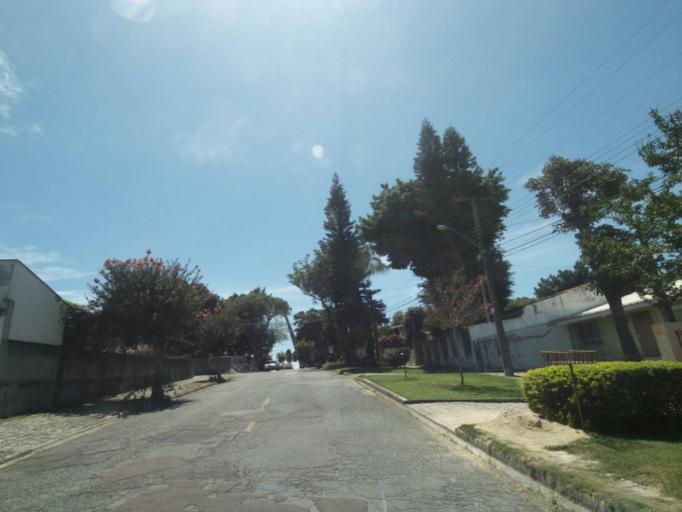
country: BR
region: Parana
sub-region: Pinhais
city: Pinhais
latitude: -25.4666
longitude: -49.2378
